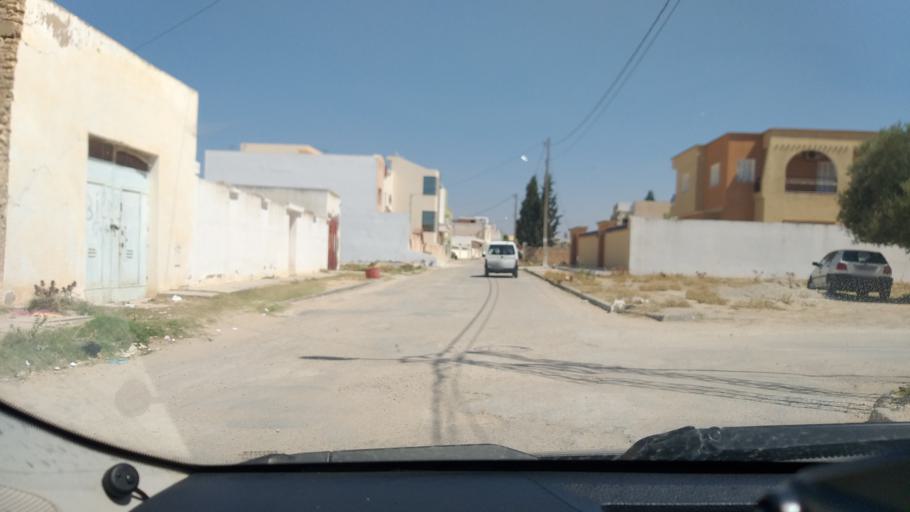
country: TN
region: Al Mahdiyah
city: El Jem
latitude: 35.2907
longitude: 10.7162
